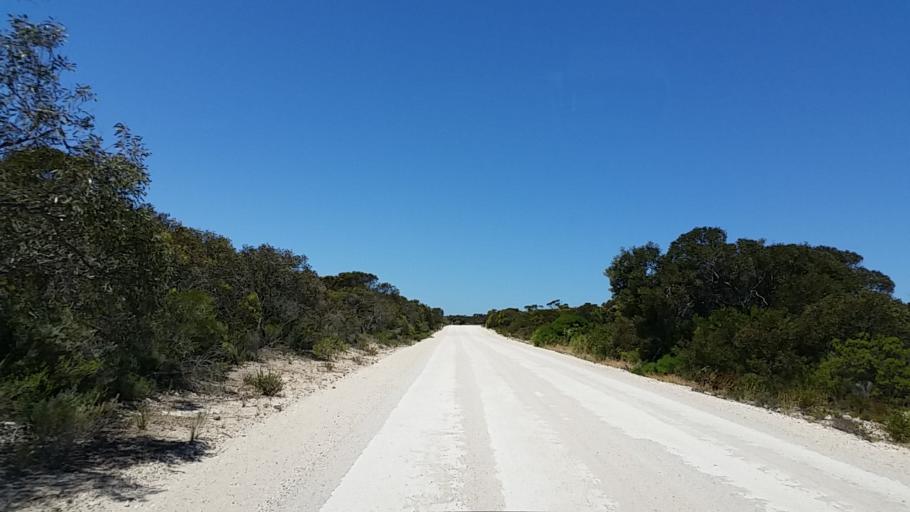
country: AU
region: South Australia
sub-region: Yorke Peninsula
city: Honiton
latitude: -35.2292
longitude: 137.1305
